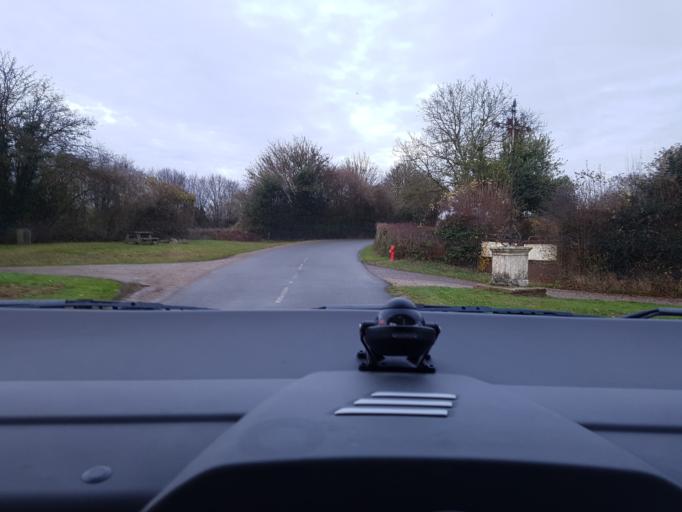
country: FR
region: Picardie
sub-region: Departement de l'Oise
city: Songeons
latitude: 49.5791
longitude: 1.8689
